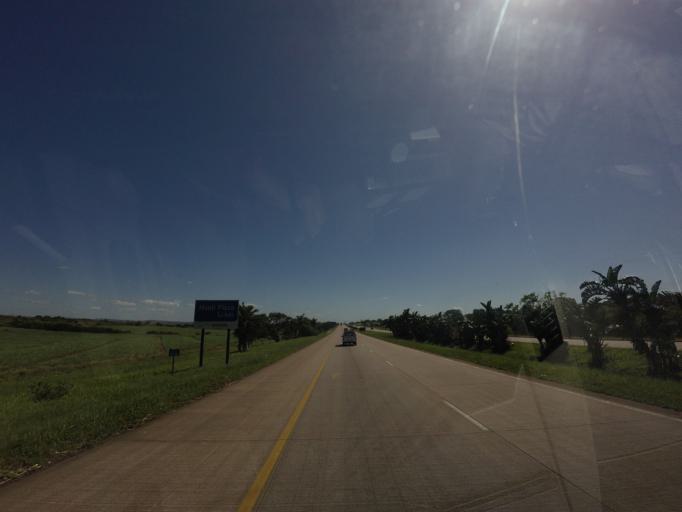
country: ZA
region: KwaZulu-Natal
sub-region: iLembe District Municipality
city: Stanger
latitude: -29.4161
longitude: 31.2769
